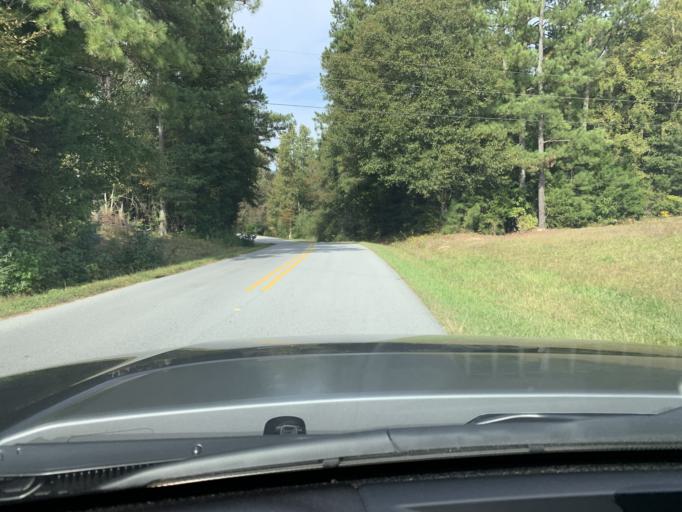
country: US
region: Georgia
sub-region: Polk County
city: Cedartown
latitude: 34.0638
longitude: -85.2350
